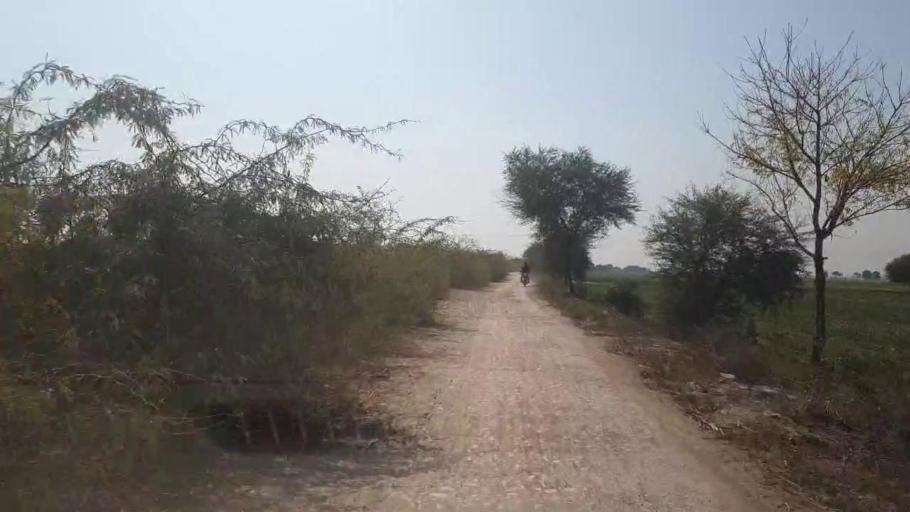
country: PK
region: Sindh
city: Chambar
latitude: 25.2409
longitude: 68.8272
